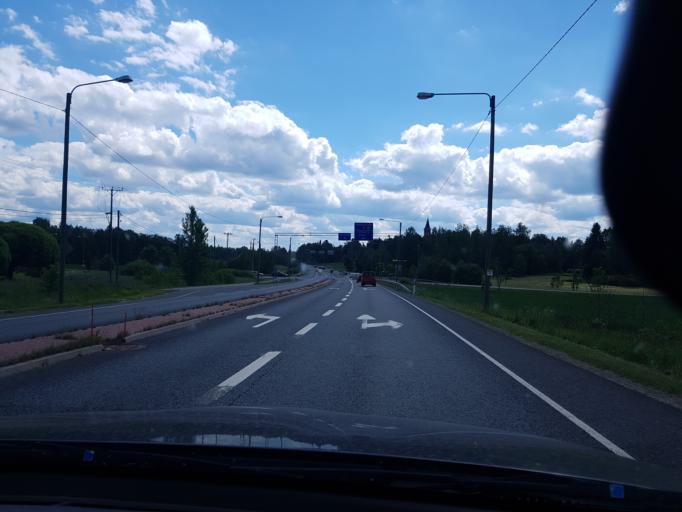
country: FI
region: Haeme
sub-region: Haemeenlinna
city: Parola
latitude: 61.0745
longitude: 24.3916
